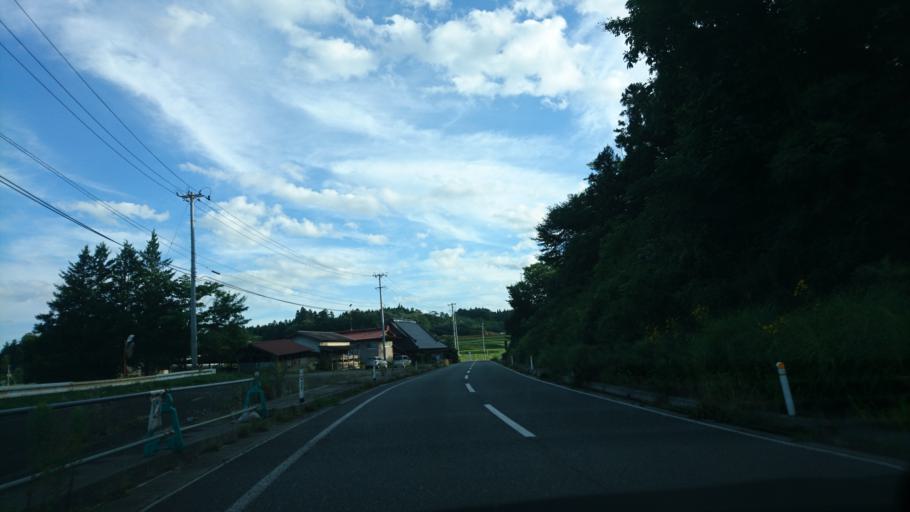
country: JP
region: Iwate
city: Ichinoseki
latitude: 38.8687
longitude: 141.1965
